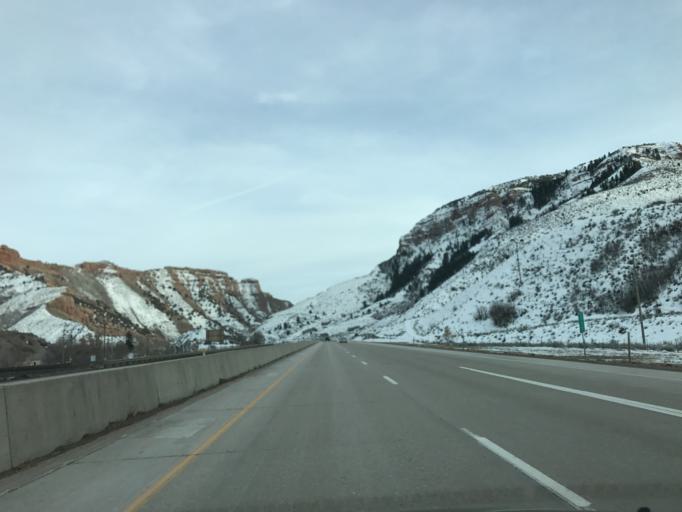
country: US
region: Utah
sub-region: Morgan County
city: Morgan
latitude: 41.0624
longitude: -111.5451
